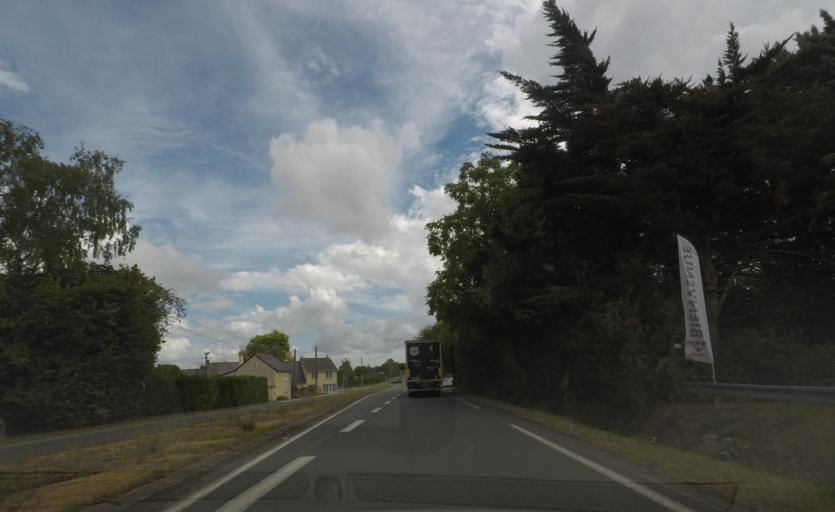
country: FR
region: Pays de la Loire
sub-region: Departement de Maine-et-Loire
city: Corze
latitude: 47.5570
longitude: -0.3782
